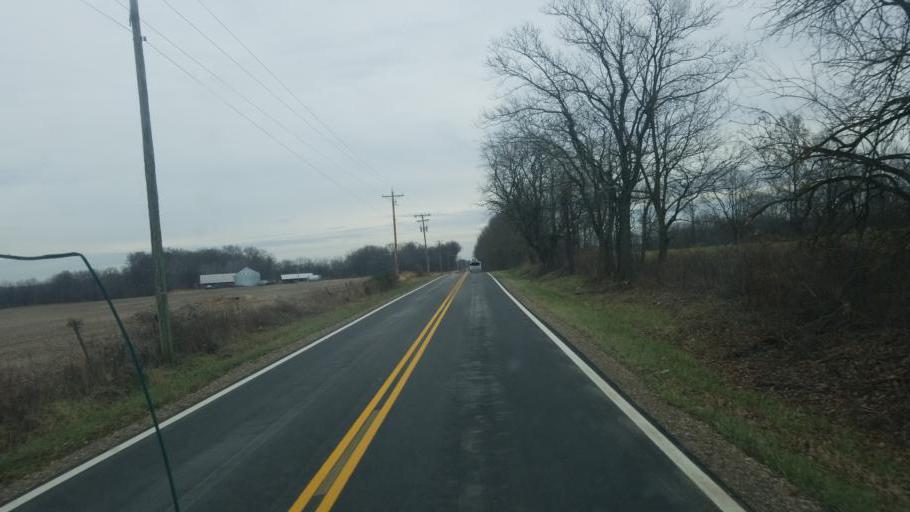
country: US
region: Ohio
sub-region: Knox County
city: Centerburg
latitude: 40.2653
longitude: -82.5820
